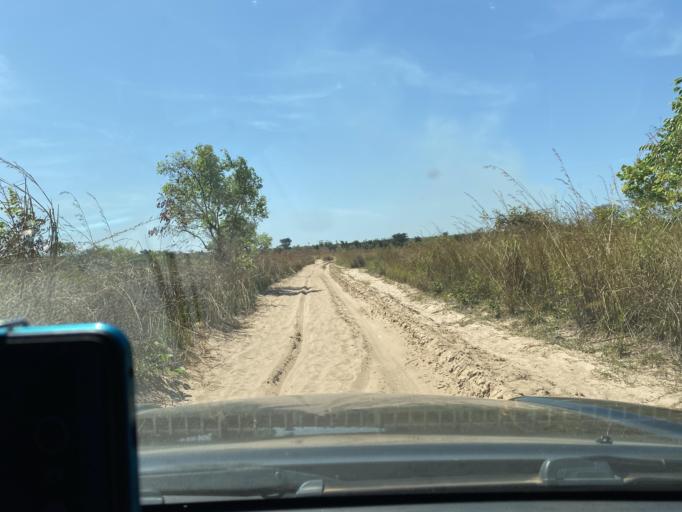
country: CD
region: Kasai-Oriental
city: Kabinda
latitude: -5.9320
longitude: 24.8314
